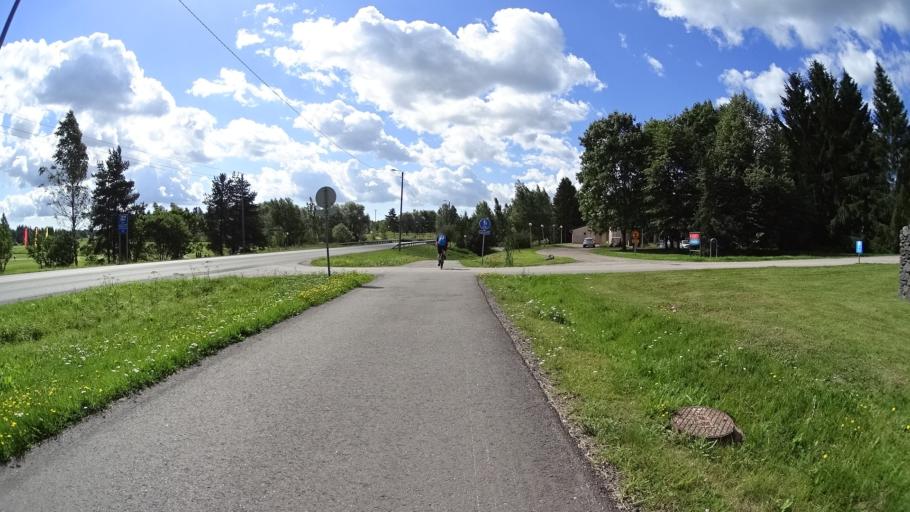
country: FI
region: Uusimaa
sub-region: Helsinki
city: Tuusula
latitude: 60.4175
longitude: 25.0523
